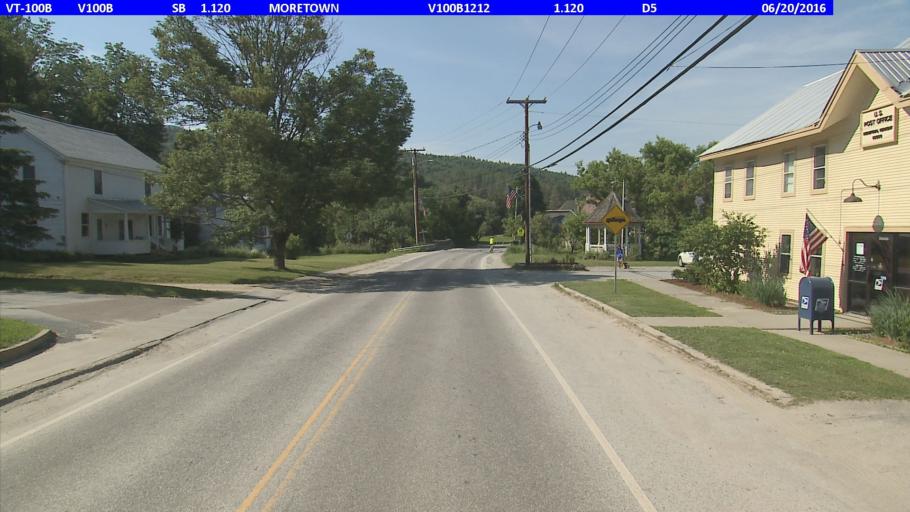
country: US
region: Vermont
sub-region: Washington County
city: Waterbury
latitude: 44.2502
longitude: -72.7615
